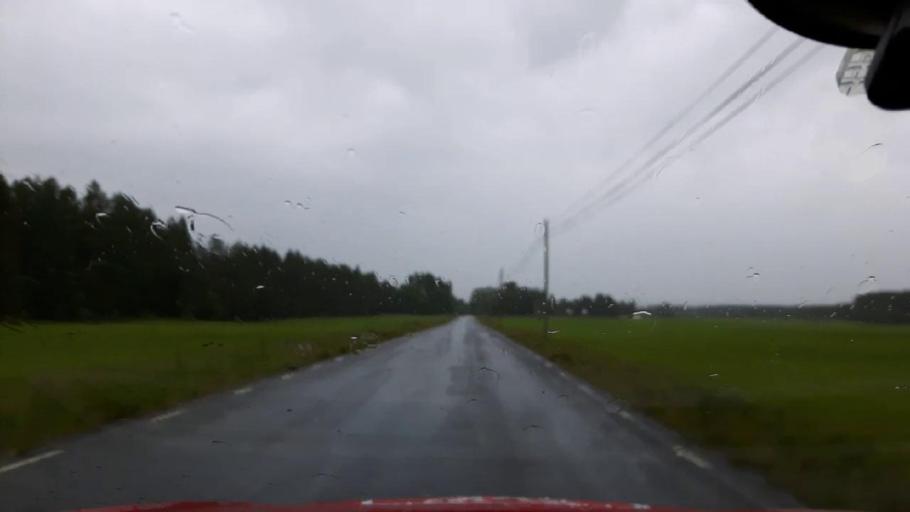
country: SE
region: Jaemtland
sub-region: OEstersunds Kommun
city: Brunflo
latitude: 62.9968
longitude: 14.7713
